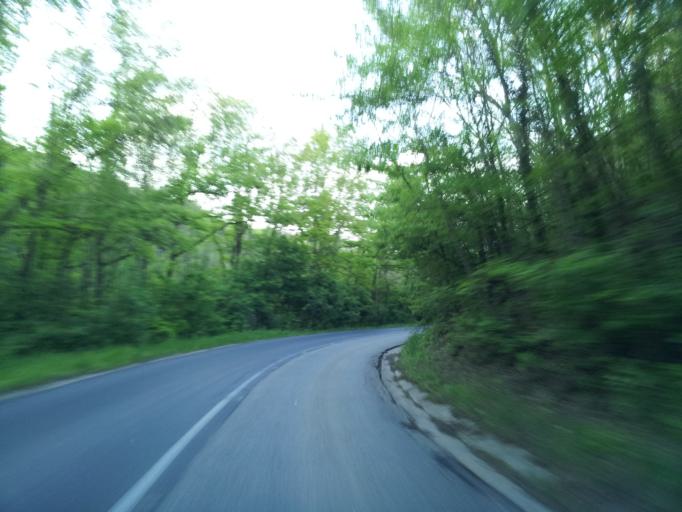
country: HU
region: Pest
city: Piliscsaba
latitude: 47.6268
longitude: 18.8061
